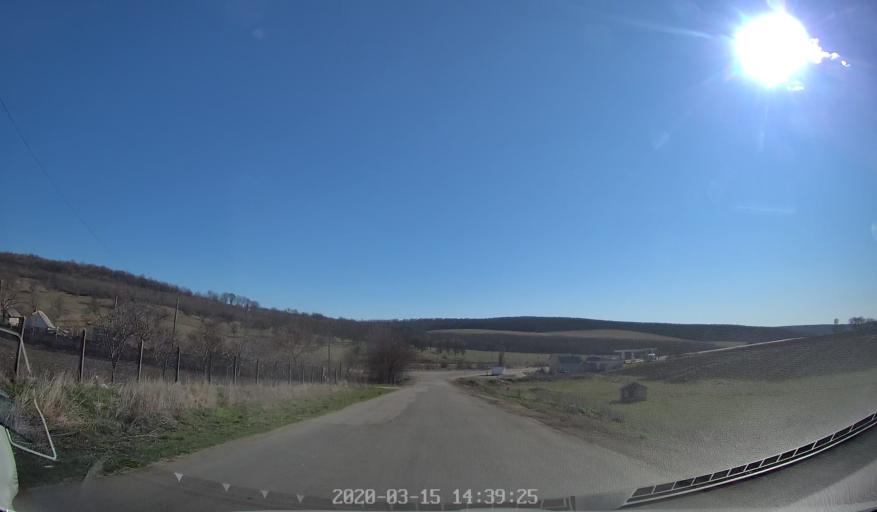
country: MD
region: Orhei
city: Orhei
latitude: 47.3019
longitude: 28.9157
